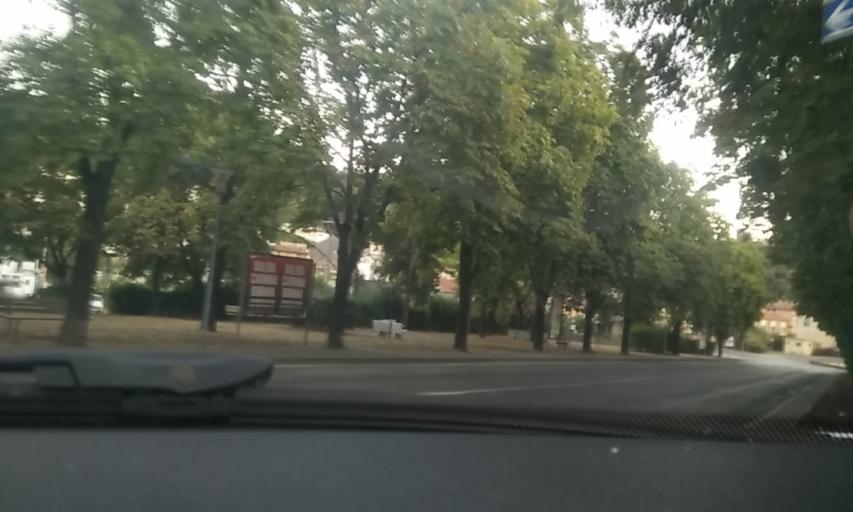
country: IT
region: Tuscany
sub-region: Provincia di Massa-Carrara
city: Carrara
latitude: 44.0760
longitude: 10.0933
